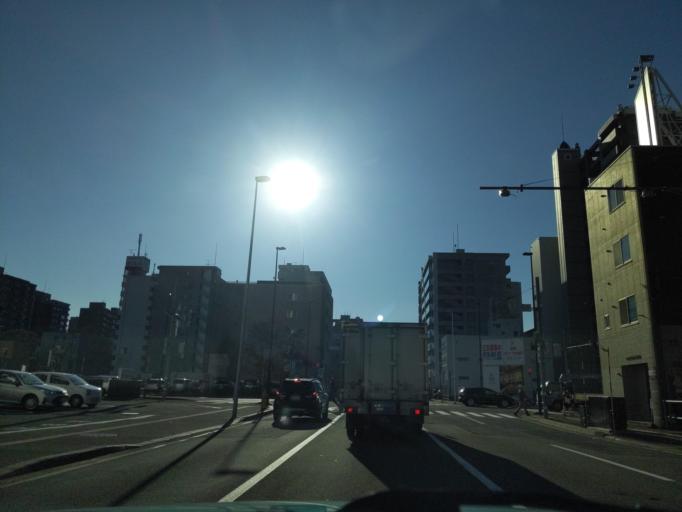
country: JP
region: Hokkaido
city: Sapporo
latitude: 43.0648
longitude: 141.3333
